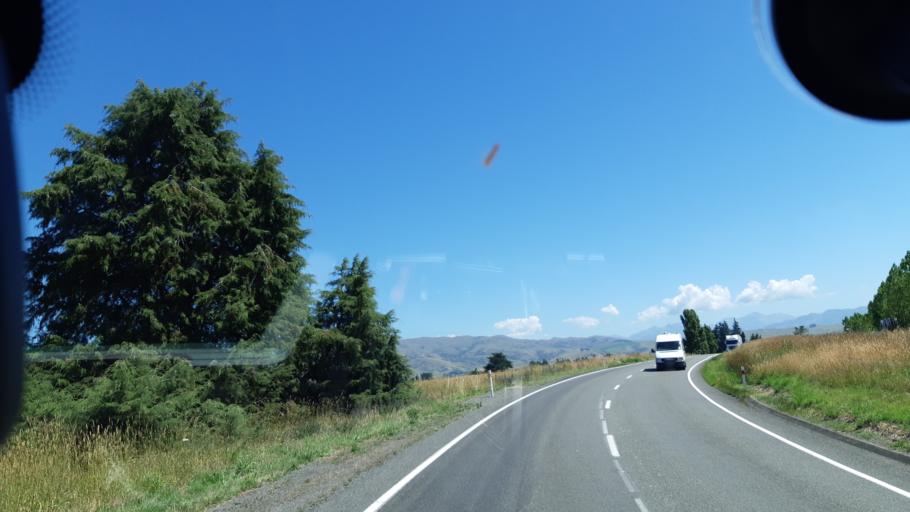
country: NZ
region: Canterbury
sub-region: Kaikoura District
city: Kaikoura
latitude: -42.7502
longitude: 173.2690
